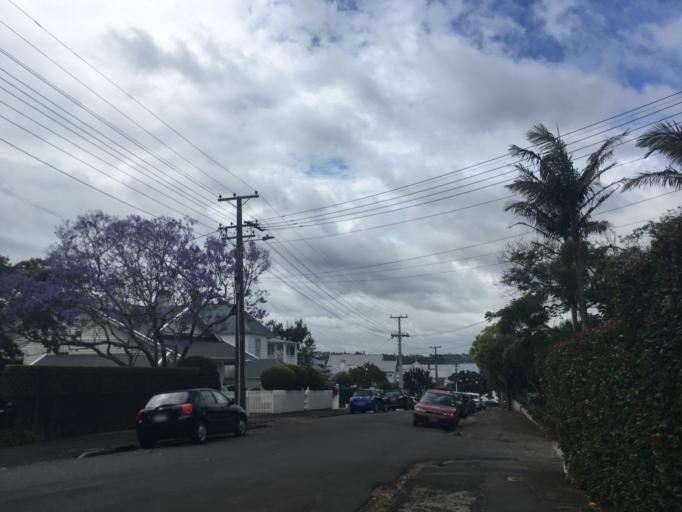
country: NZ
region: Auckland
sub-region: Auckland
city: Auckland
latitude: -36.8300
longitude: 174.8006
